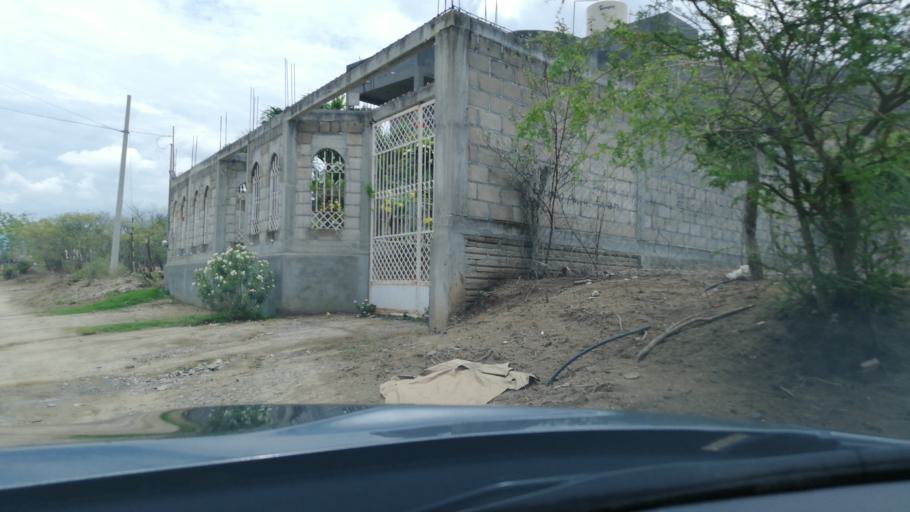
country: MX
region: Oaxaca
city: Santa Maria Jalapa del Marques
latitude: 16.4505
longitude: -95.4424
